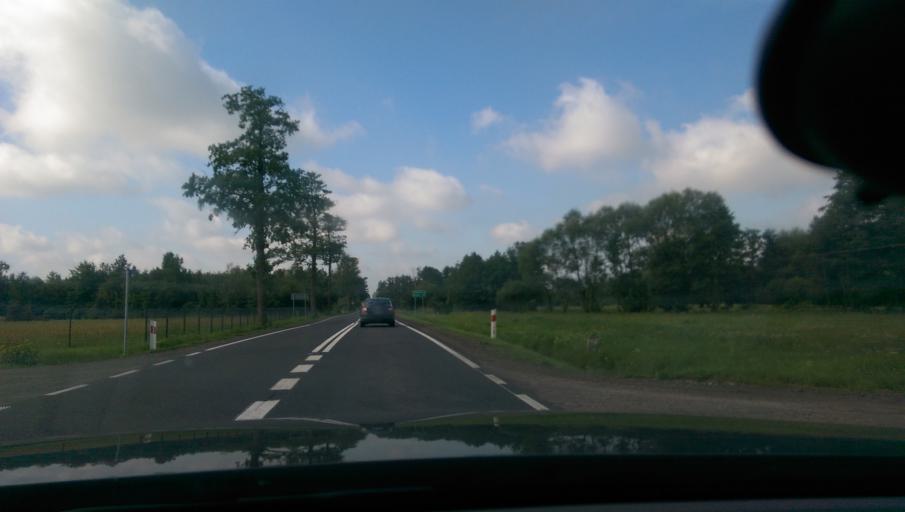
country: PL
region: Masovian Voivodeship
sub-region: Powiat ciechanowski
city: Ojrzen
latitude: 52.7256
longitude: 20.5094
